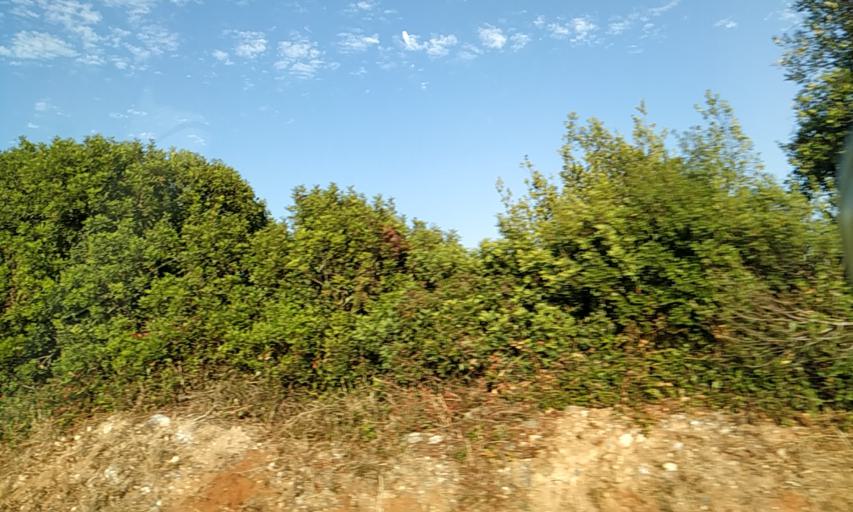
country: PT
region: Santarem
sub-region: Alcanena
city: Alcanena
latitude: 39.4026
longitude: -8.6413
